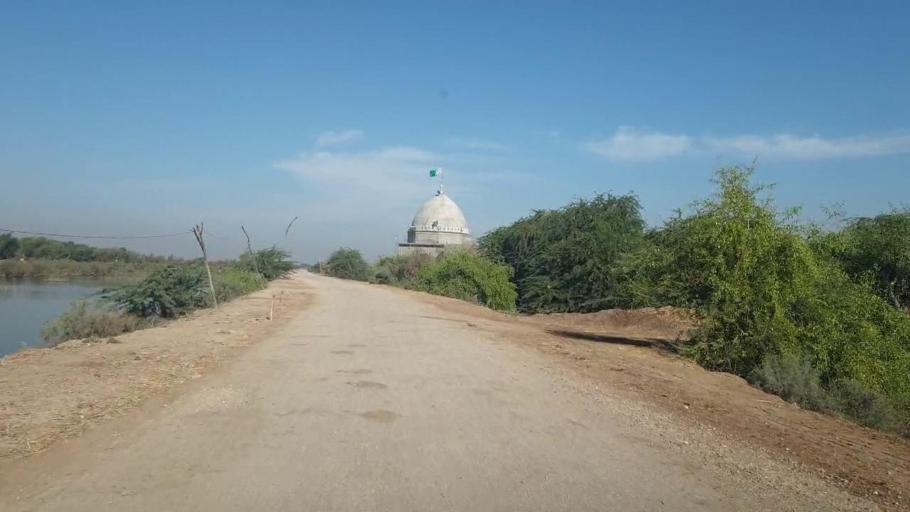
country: PK
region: Sindh
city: Talhar
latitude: 24.9139
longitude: 68.8056
